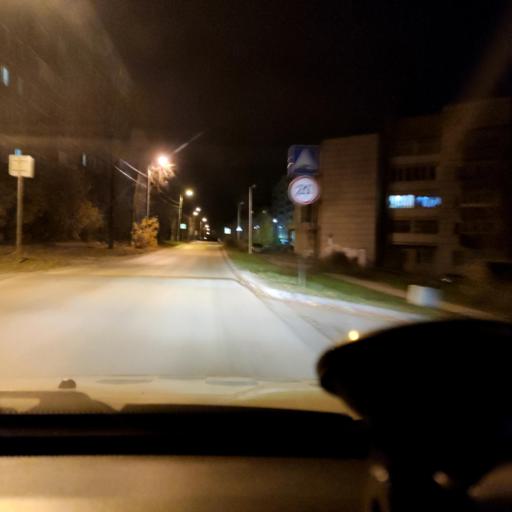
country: RU
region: Perm
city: Perm
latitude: 58.1020
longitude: 56.3035
